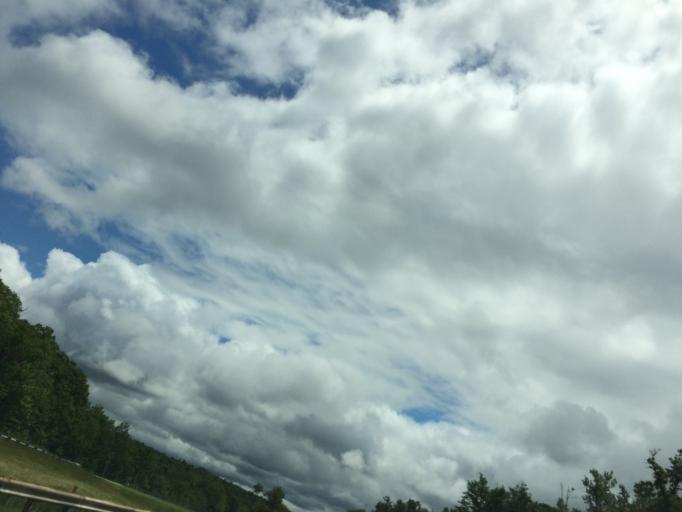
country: US
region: Massachusetts
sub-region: Berkshire County
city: Otis
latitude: 42.2401
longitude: -73.0649
